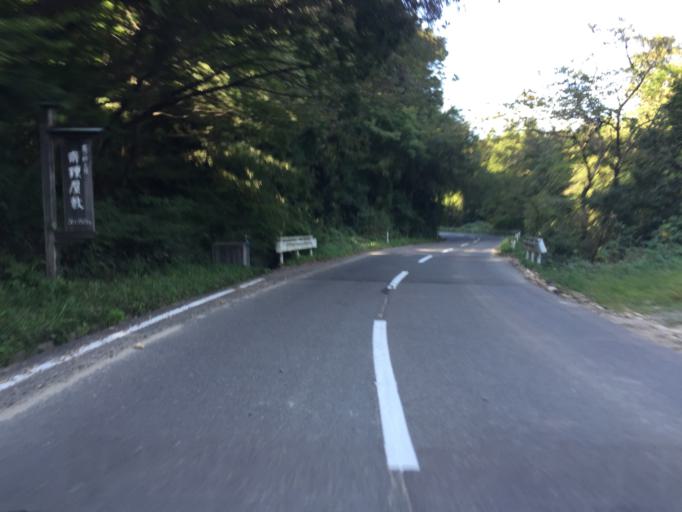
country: JP
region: Miyagi
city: Marumori
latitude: 37.8738
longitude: 140.7812
